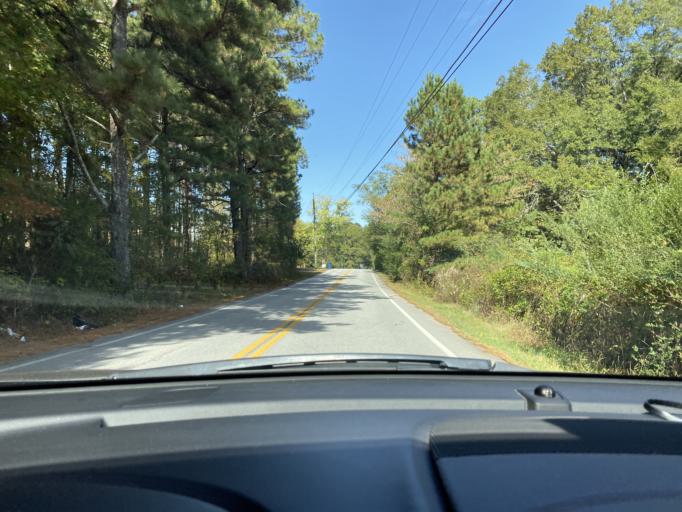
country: US
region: Georgia
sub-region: Walton County
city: Loganville
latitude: 33.8726
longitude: -83.9108
